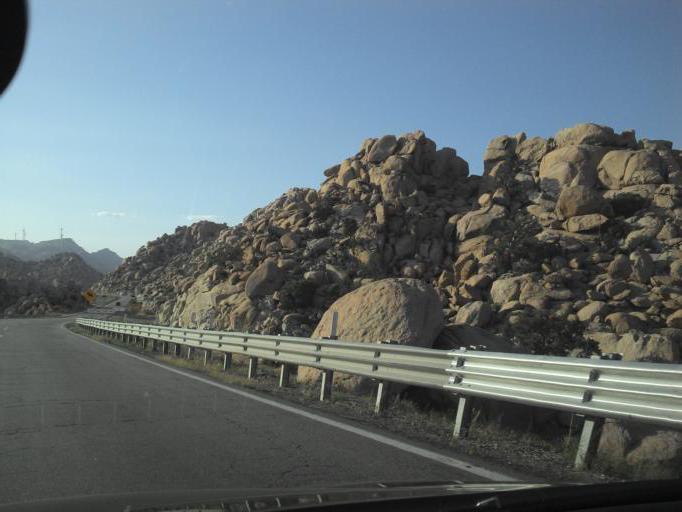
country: MX
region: Baja California
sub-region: Tecate
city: Cereso del Hongo
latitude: 32.5588
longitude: -116.0351
